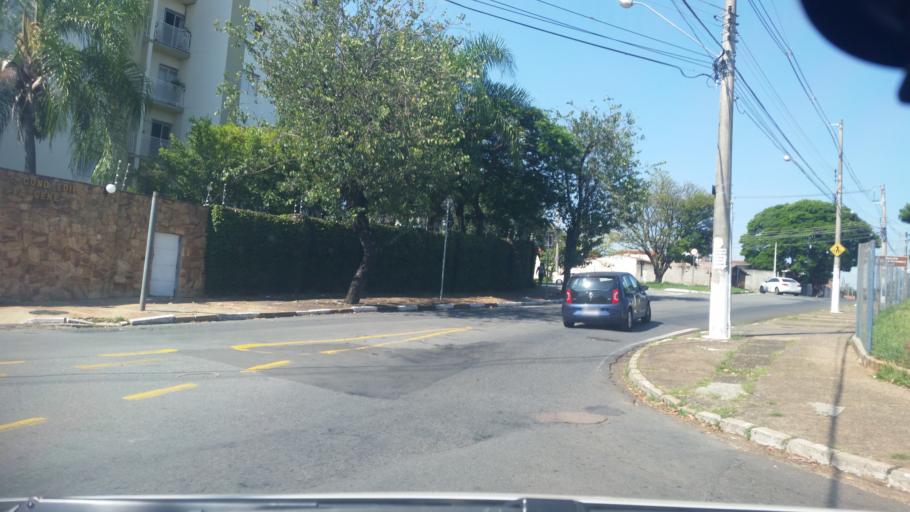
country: BR
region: Sao Paulo
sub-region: Campinas
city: Campinas
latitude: -22.8523
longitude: -47.0692
